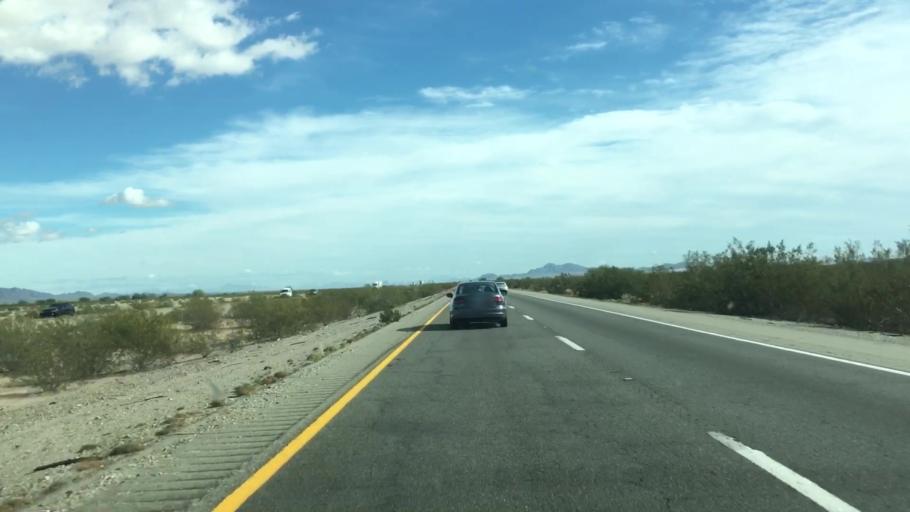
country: US
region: California
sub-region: Riverside County
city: Mesa Verde
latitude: 33.6193
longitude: -115.0305
